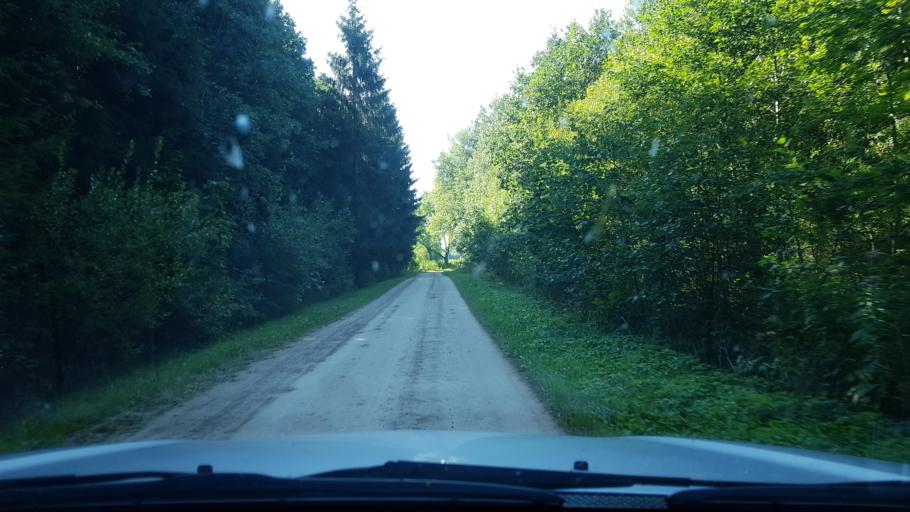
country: EE
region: Ida-Virumaa
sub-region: Toila vald
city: Voka
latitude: 59.3844
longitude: 27.6654
